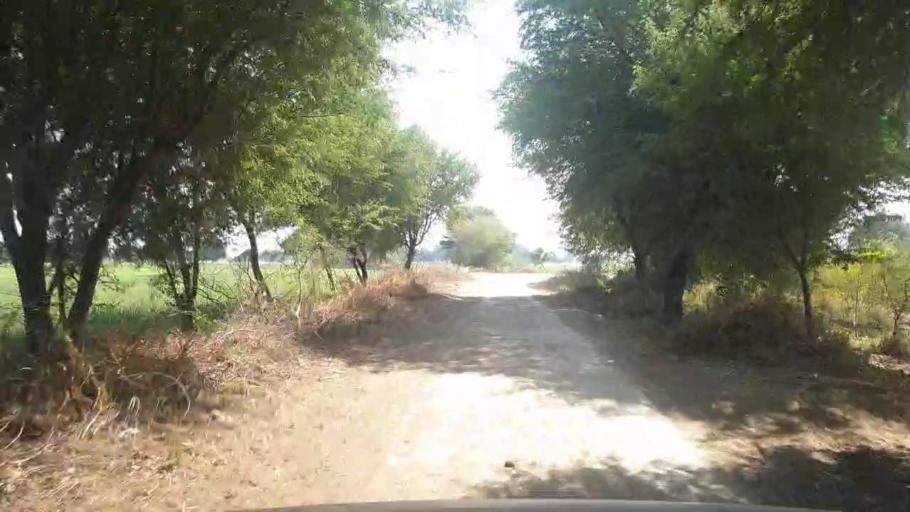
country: PK
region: Sindh
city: Chambar
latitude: 25.2729
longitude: 68.8140
